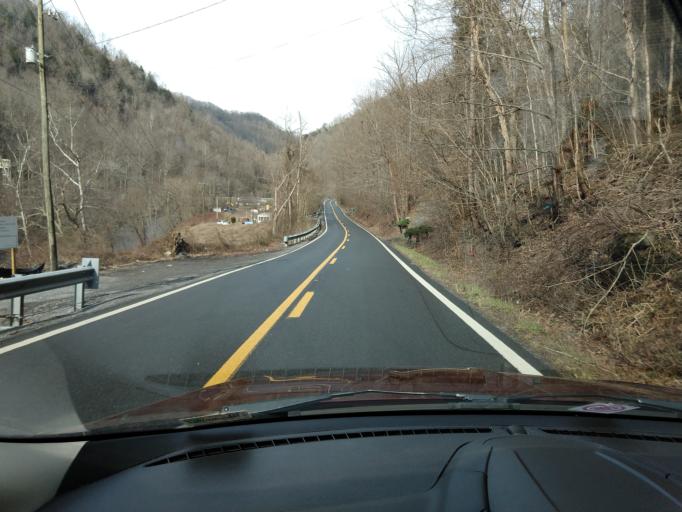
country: US
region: West Virginia
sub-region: McDowell County
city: Welch
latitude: 37.3447
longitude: -81.7424
